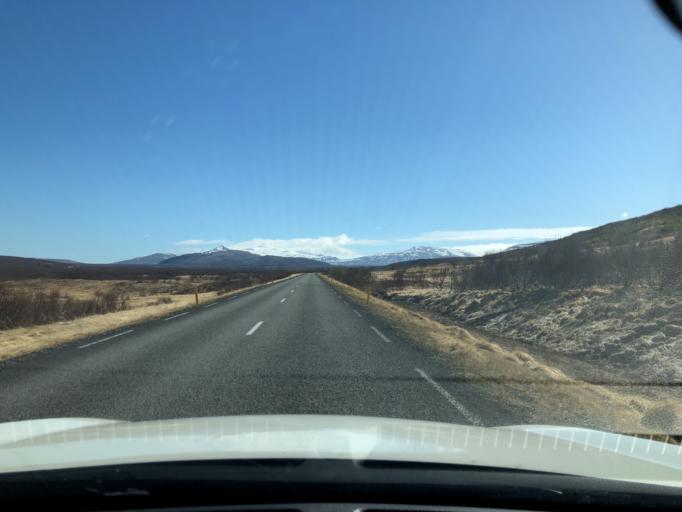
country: IS
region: South
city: Hveragerdi
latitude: 64.7010
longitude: -21.0231
